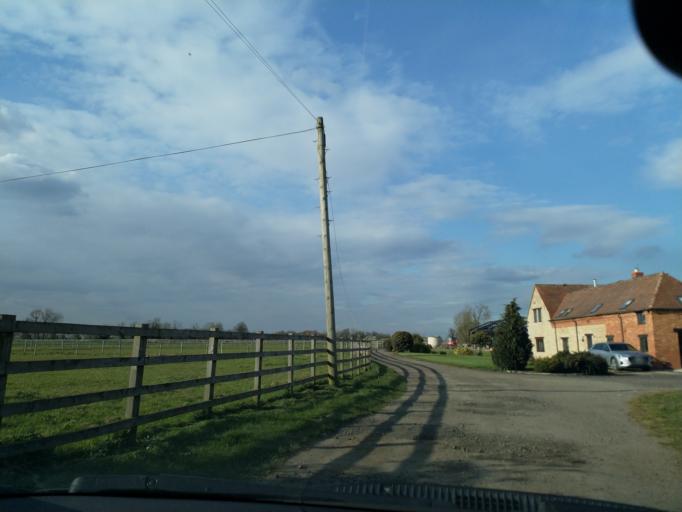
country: GB
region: England
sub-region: Warwickshire
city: Wellesbourne Mountford
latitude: 52.2107
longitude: -1.5208
